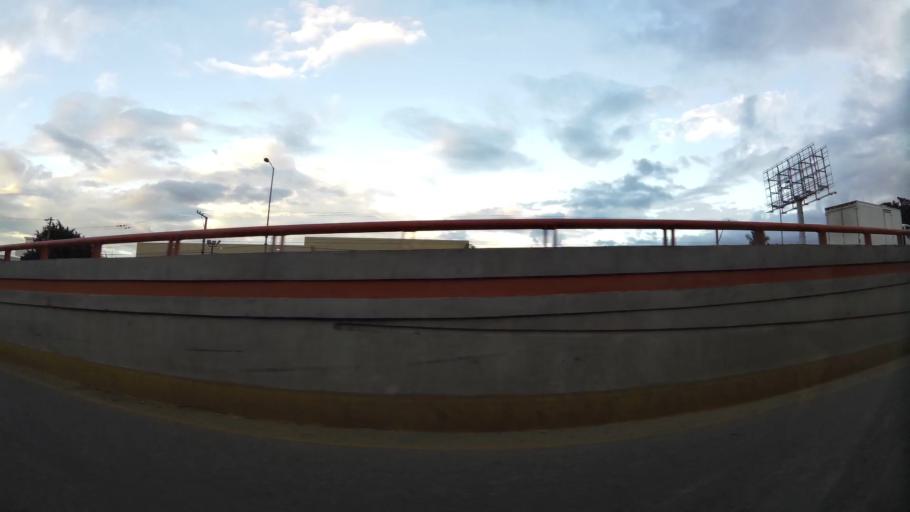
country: DO
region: Santo Domingo
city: Santo Domingo Oeste
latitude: 18.5238
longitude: -70.0107
